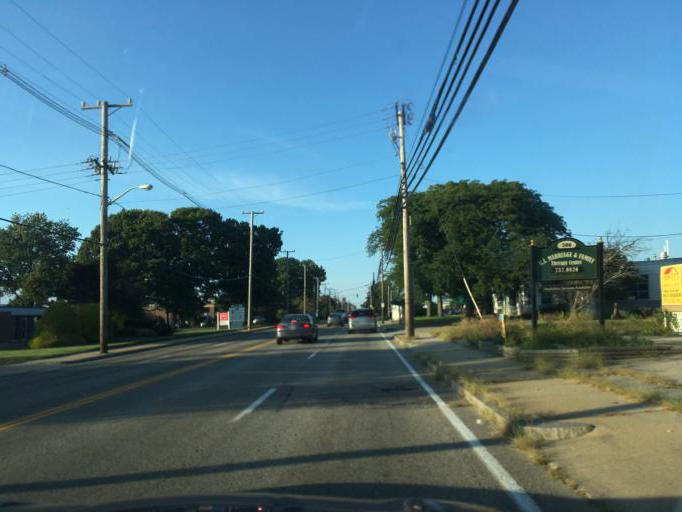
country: US
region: Rhode Island
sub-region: Kent County
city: Warwick
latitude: 41.7338
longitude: -71.4411
